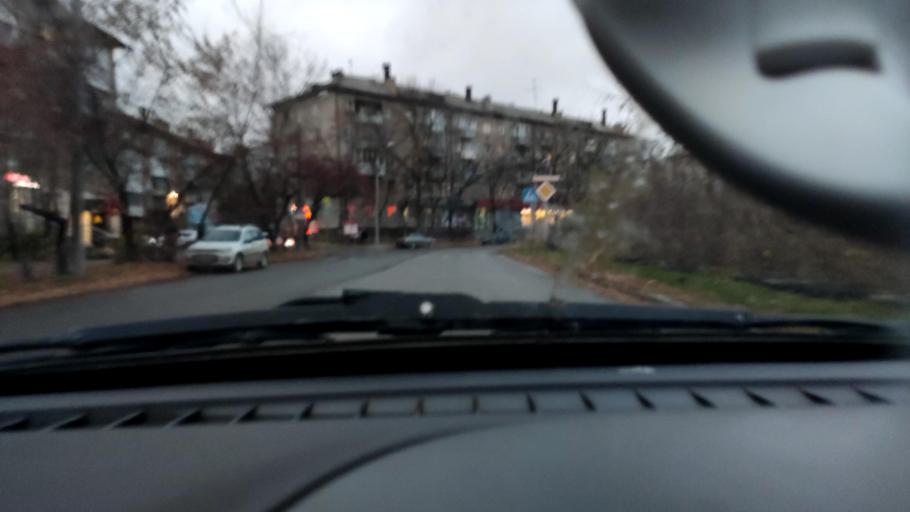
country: RU
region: Perm
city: Kondratovo
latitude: 58.0469
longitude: 56.0926
